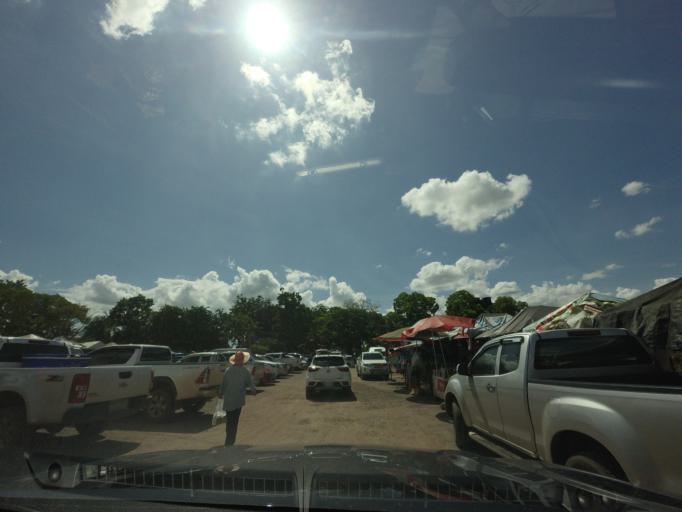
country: TH
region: Changwat Udon Thani
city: Ban Dung
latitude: 17.7445
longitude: 103.3587
